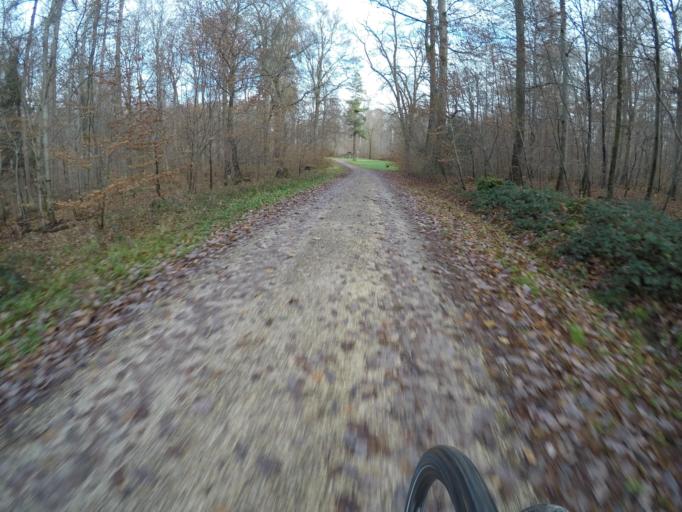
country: DE
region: Baden-Wuerttemberg
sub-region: Regierungsbezirk Stuttgart
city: Baltmannsweiler
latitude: 48.7477
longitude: 9.4261
